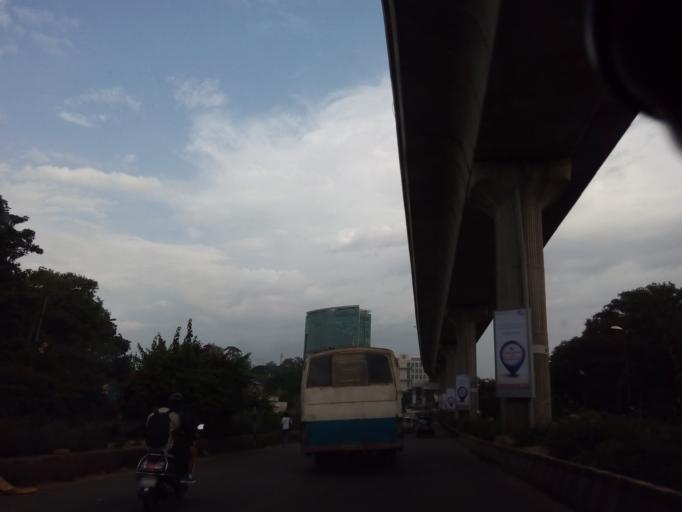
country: IN
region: Karnataka
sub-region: Bangalore Urban
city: Bangalore
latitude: 13.0185
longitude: 77.5534
